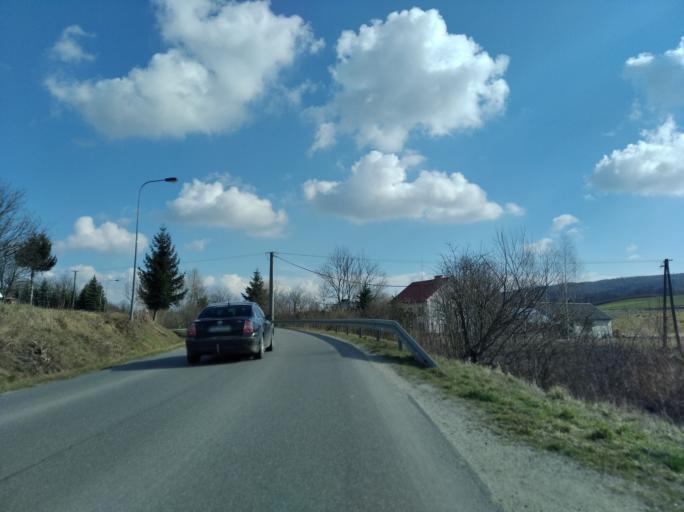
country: PL
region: Subcarpathian Voivodeship
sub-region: Powiat jasielski
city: Kolaczyce
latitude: 49.8551
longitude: 21.4932
